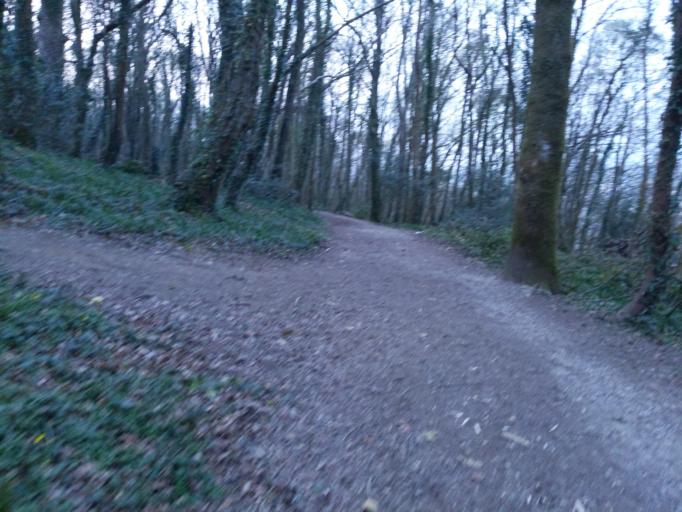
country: GB
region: England
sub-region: Plymouth
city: Plymouth
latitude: 50.4197
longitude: -4.1429
